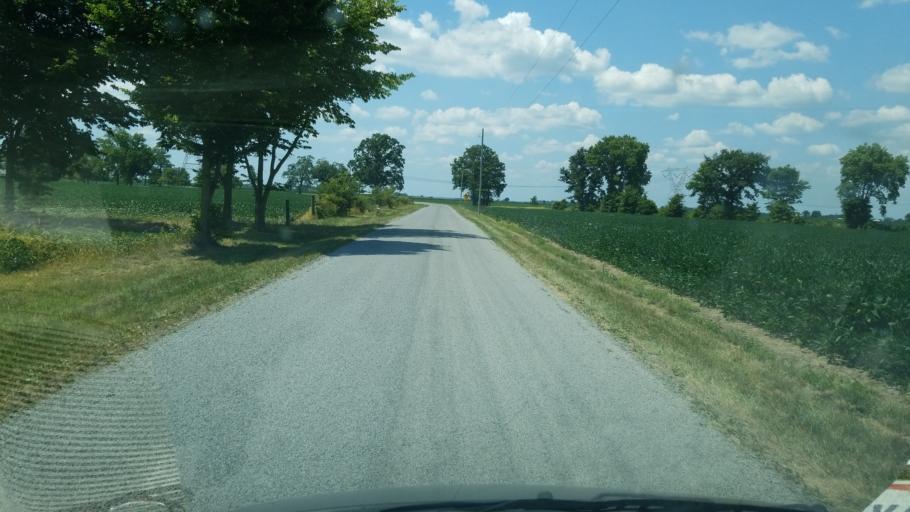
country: US
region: Ohio
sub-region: Madison County
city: Choctaw Lake
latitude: 40.0752
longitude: -83.4114
